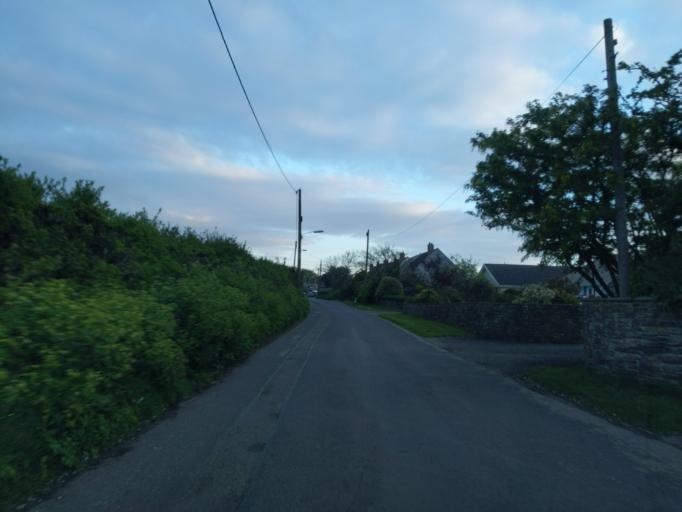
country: GB
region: England
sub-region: Cornwall
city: Polzeath
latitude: 50.5607
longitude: -4.8725
